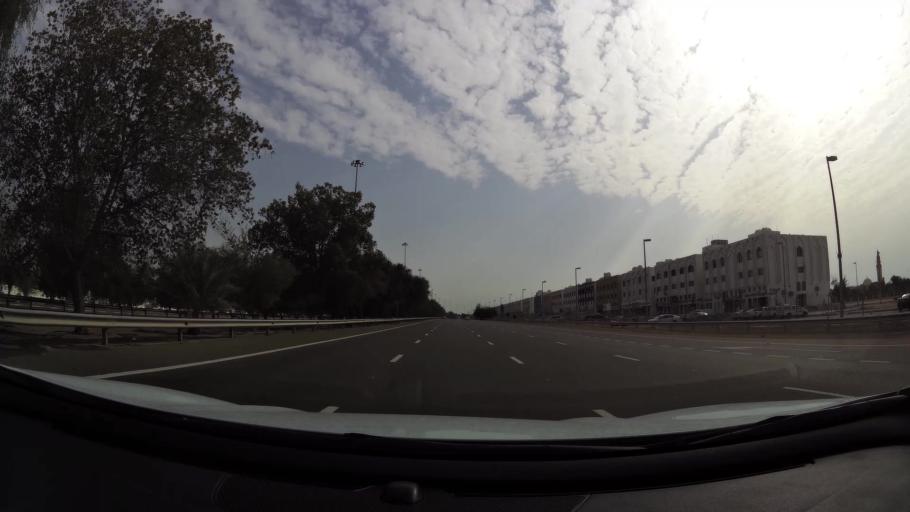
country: AE
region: Abu Dhabi
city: Abu Dhabi
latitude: 24.5305
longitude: 54.6921
